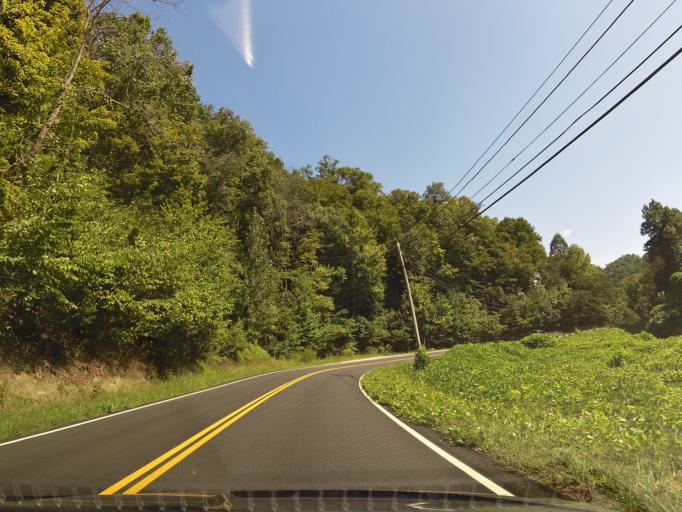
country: US
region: Kentucky
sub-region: Leslie County
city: Hyden
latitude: 37.1506
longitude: -83.3993
